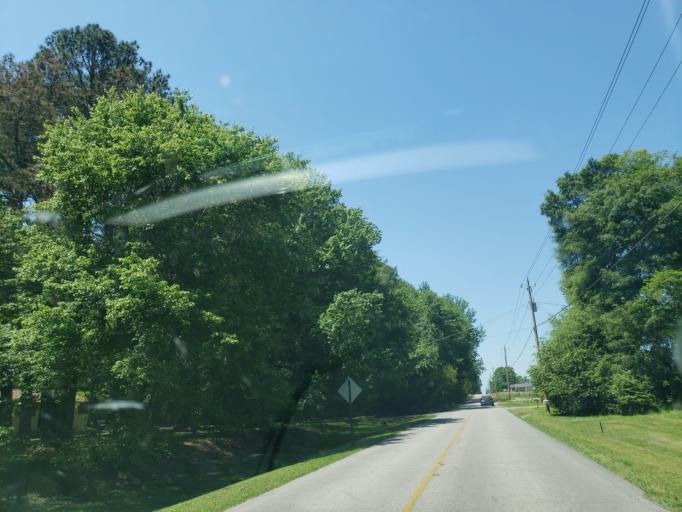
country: US
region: Alabama
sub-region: Madison County
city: Harvest
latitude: 34.9625
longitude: -86.7143
